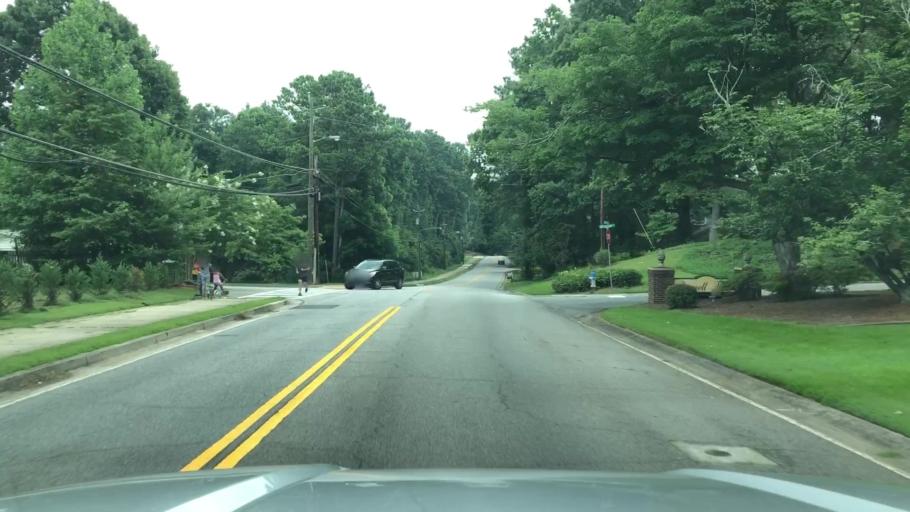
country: US
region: Georgia
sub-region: Cobb County
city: Smyrna
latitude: 33.8617
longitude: -84.5455
